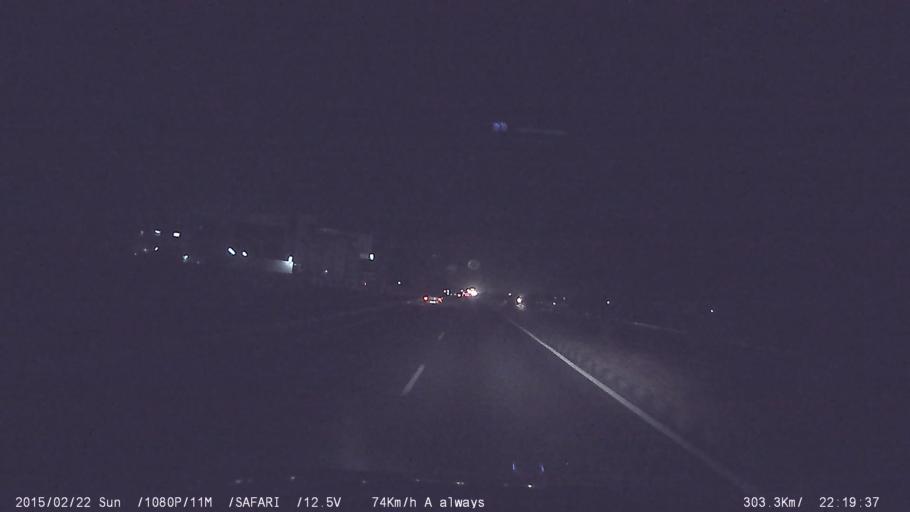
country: IN
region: Tamil Nadu
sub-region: Karur
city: Karur
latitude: 10.9819
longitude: 78.0645
